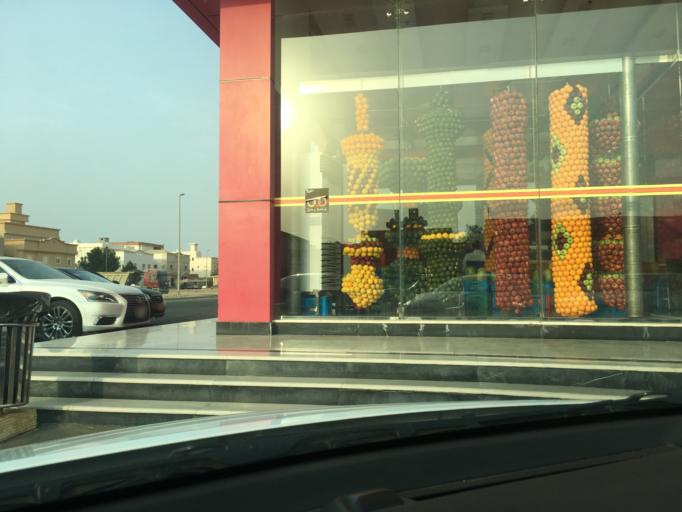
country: SA
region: Makkah
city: Jeddah
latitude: 21.7549
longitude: 39.1862
